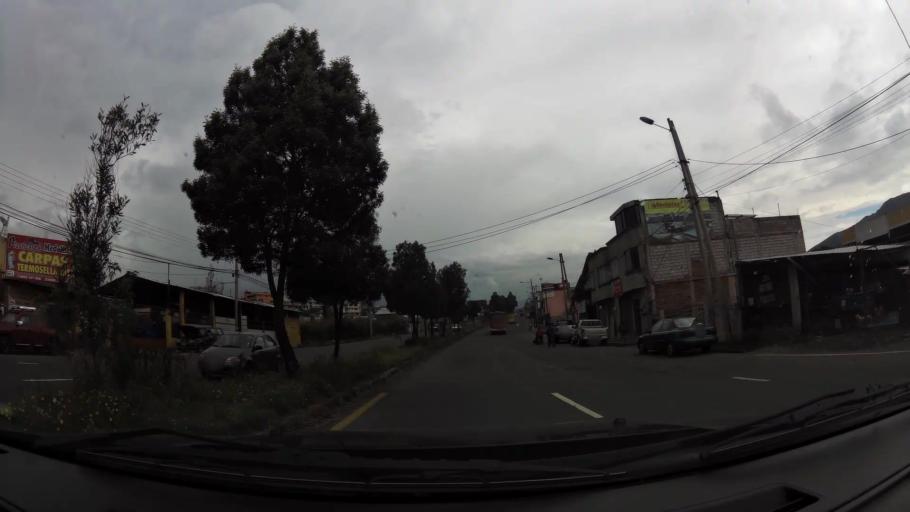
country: EC
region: Pichincha
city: Sangolqui
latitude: -0.3606
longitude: -78.5491
